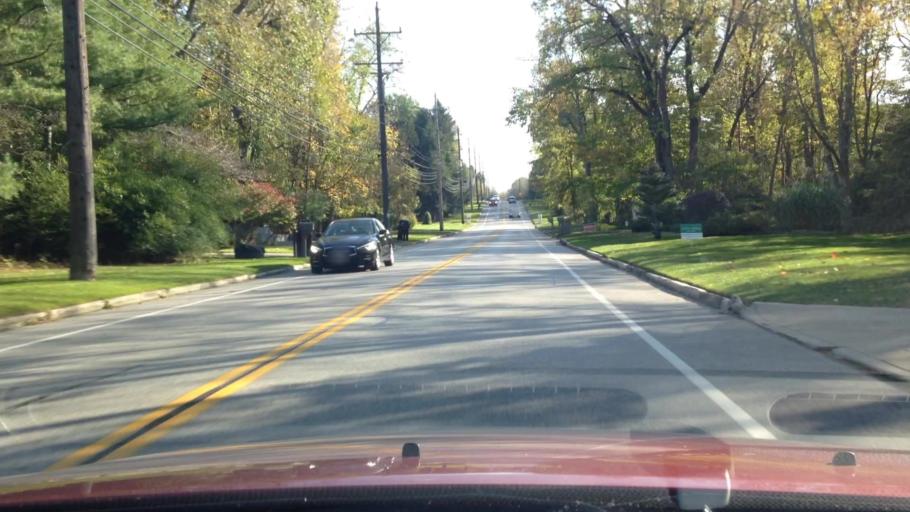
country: US
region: Ohio
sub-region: Cuyahoga County
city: Pepper Pike
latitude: 41.4713
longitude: -81.4635
